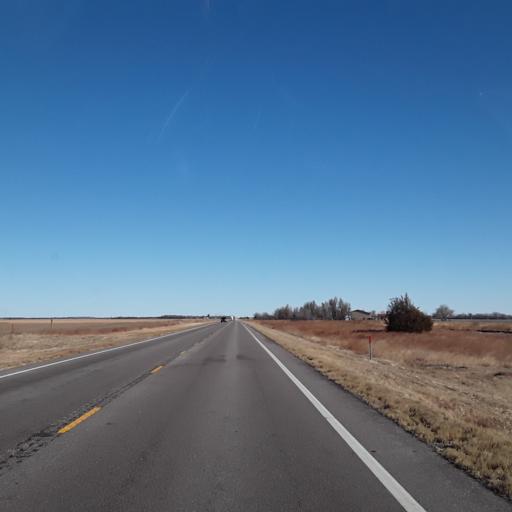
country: US
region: Kansas
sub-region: Pawnee County
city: Larned
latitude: 38.0937
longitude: -99.2171
